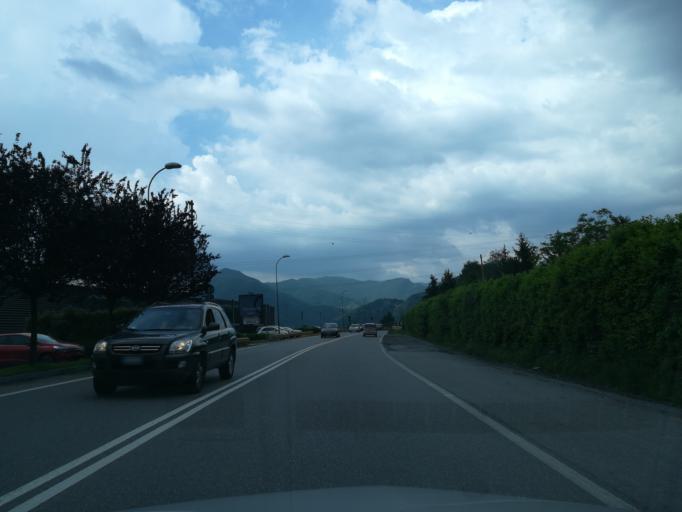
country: IT
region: Lombardy
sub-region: Provincia di Bergamo
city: Paladina
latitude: 45.7365
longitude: 9.6086
